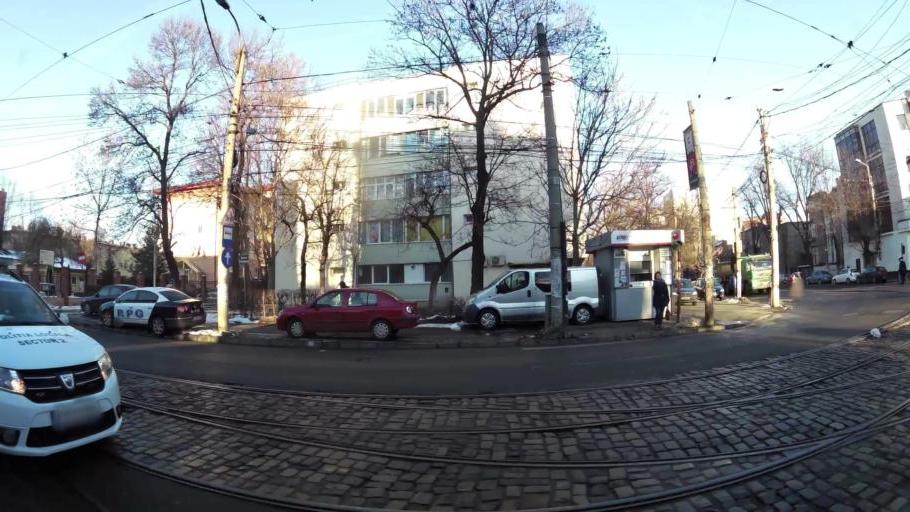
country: RO
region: Bucuresti
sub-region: Municipiul Bucuresti
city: Bucharest
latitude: 44.4464
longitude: 26.1346
